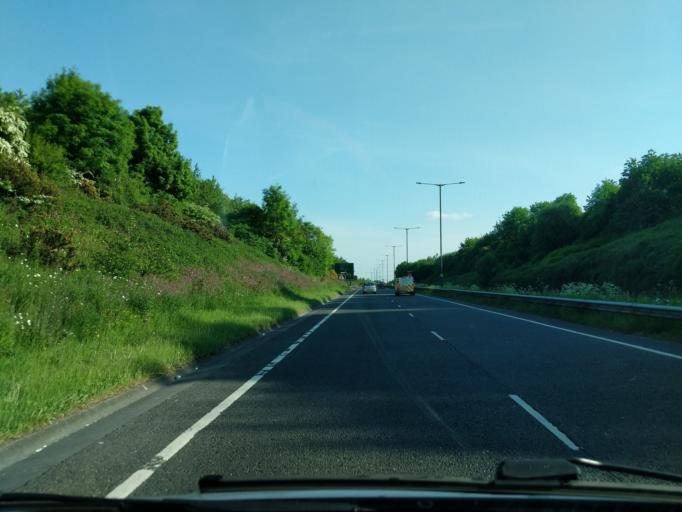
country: GB
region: England
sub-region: St. Helens
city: St Helens
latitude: 53.4322
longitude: -2.7399
